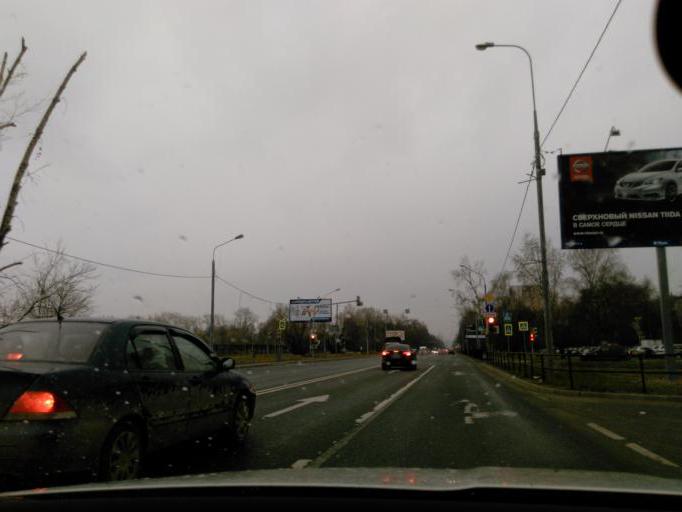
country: RU
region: Moscow
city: Khimki
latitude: 55.8664
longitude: 37.4471
